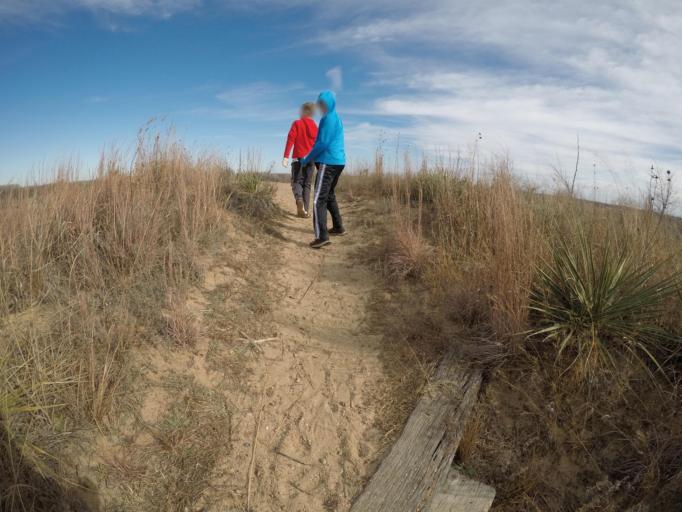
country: US
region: Kansas
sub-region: Reno County
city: Buhler
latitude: 38.1177
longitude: -97.8577
